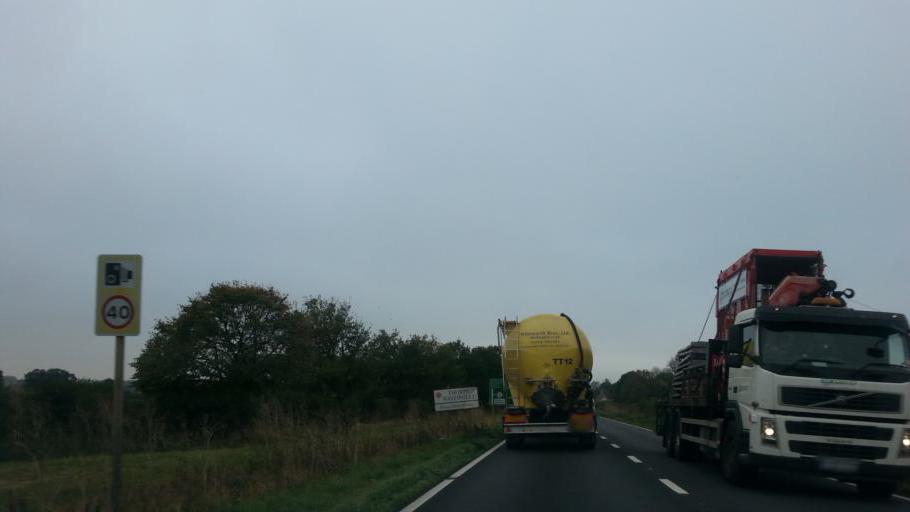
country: GB
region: England
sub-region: Northamptonshire
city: Thrapston
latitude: 52.4251
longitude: -0.4908
